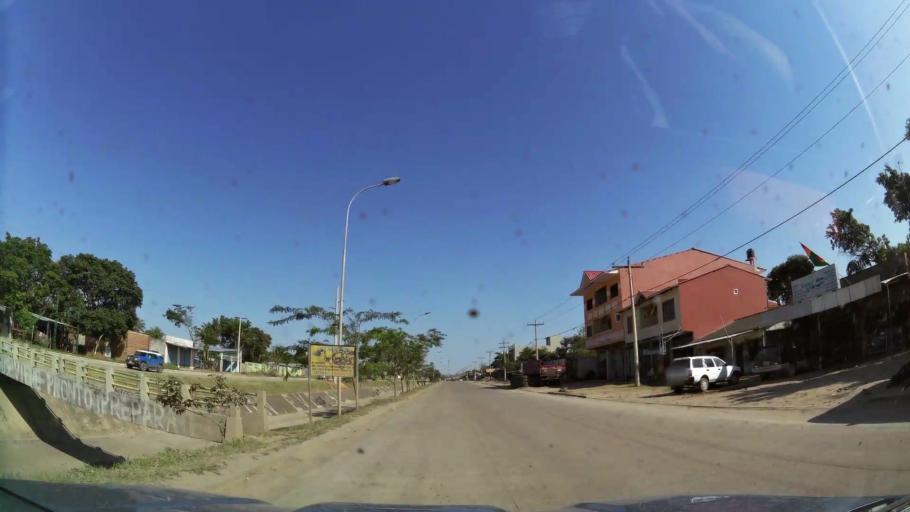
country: BO
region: Santa Cruz
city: Cotoca
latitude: -17.8082
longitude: -63.1095
